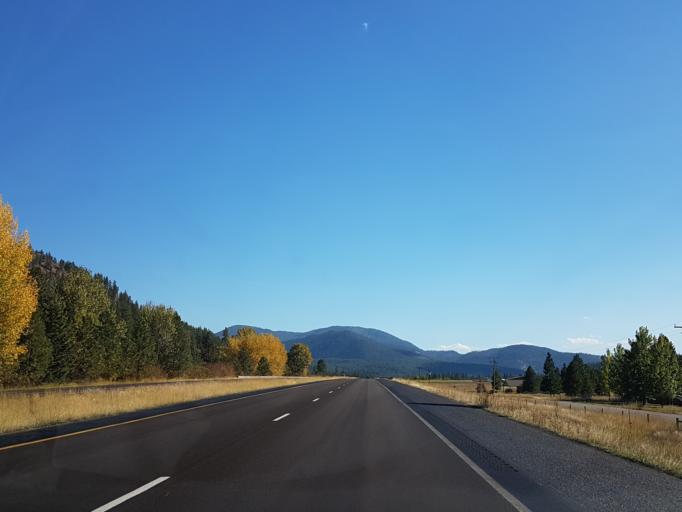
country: US
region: Montana
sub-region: Mineral County
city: Superior
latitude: 47.1438
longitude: -114.8158
